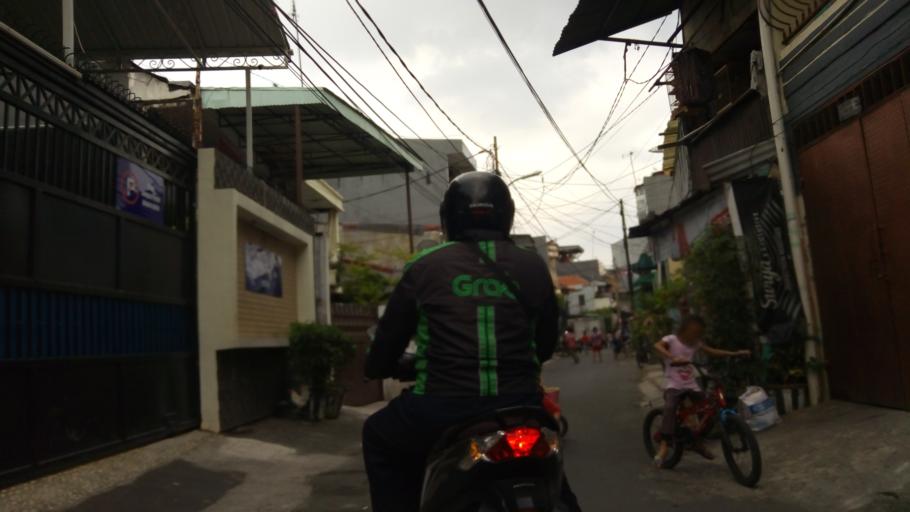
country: ID
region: Jakarta Raya
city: Jakarta
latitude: -6.1529
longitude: 106.8322
